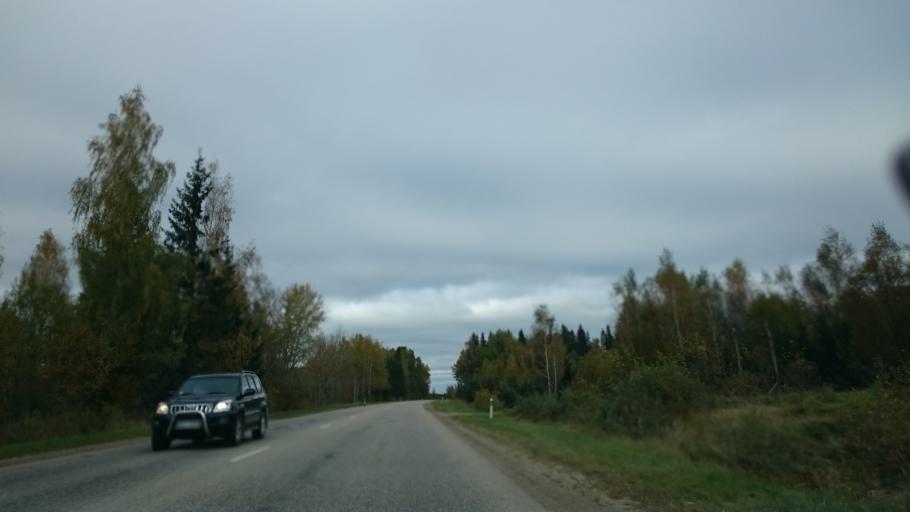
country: LV
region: Amatas Novads
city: Drabesi
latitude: 57.2378
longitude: 25.2541
